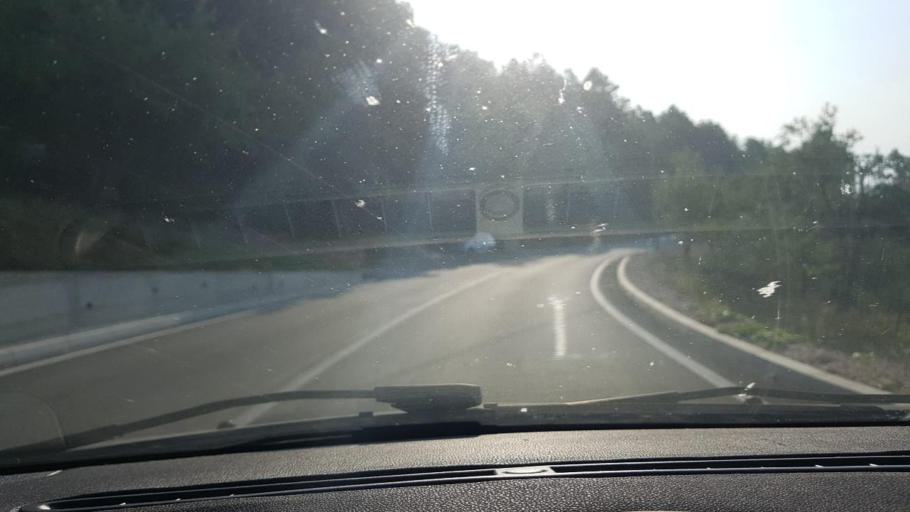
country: BA
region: Federation of Bosnia and Herzegovina
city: Prozor
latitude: 43.7969
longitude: 17.6303
